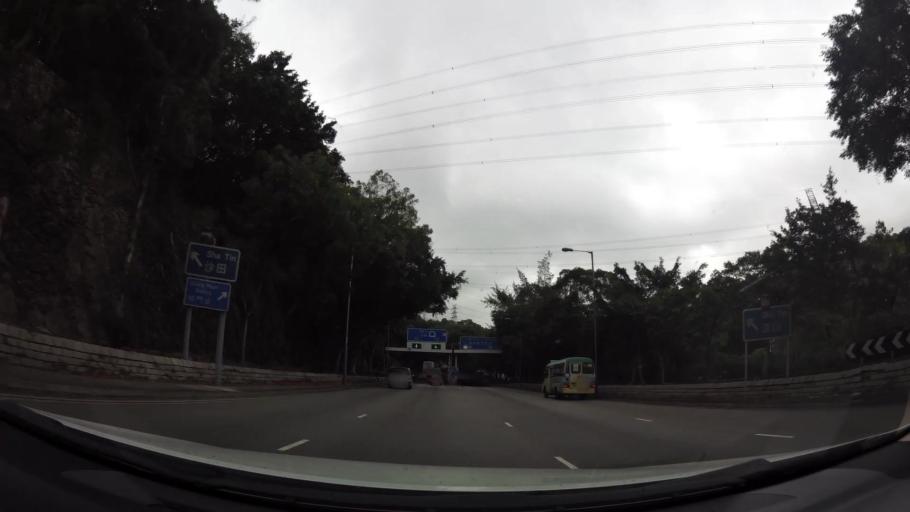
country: HK
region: Tsuen Wan
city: Tsuen Wan
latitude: 22.3804
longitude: 114.1319
